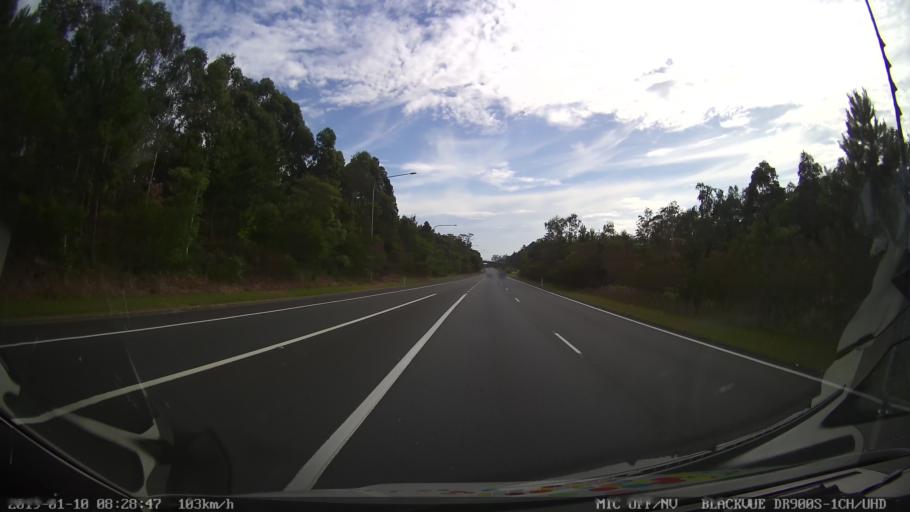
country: AU
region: New South Wales
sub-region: Coffs Harbour
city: Bonville
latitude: -30.3891
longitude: 153.0367
